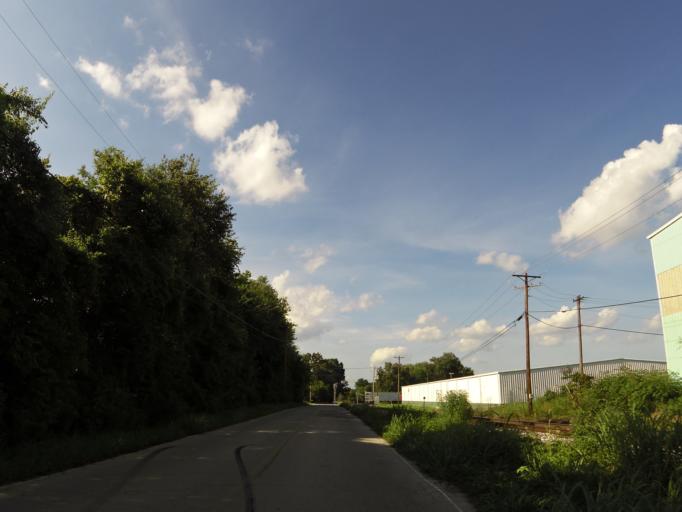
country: US
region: Tennessee
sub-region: Blount County
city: Eagleton Village
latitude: 35.8271
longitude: -83.9546
